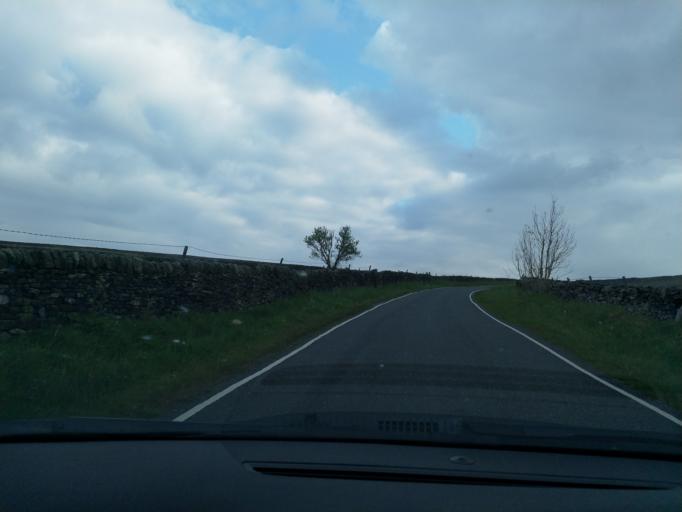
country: GB
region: England
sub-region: Derbyshire
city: Hathersage
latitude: 53.3375
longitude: -1.6336
